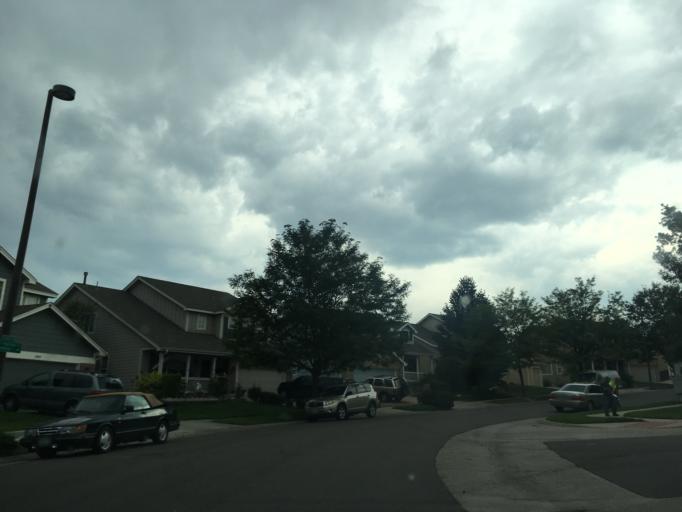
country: US
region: Colorado
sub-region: Arapahoe County
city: Sheridan
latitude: 39.6556
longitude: -105.0369
